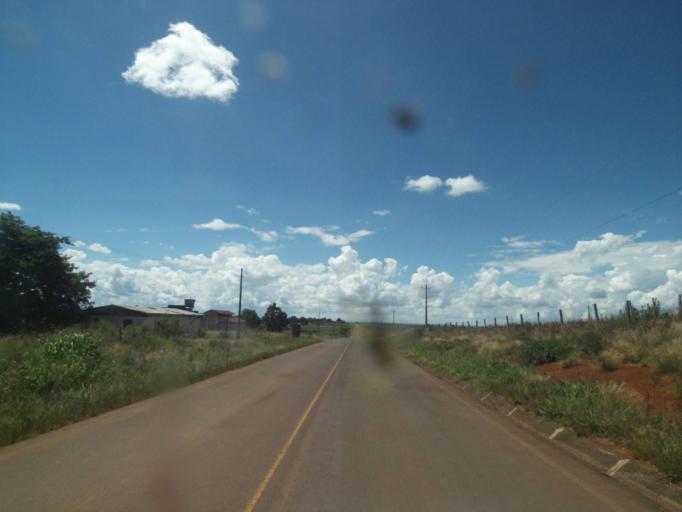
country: BR
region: Parana
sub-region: Pinhao
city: Pinhao
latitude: -25.8220
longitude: -52.0409
